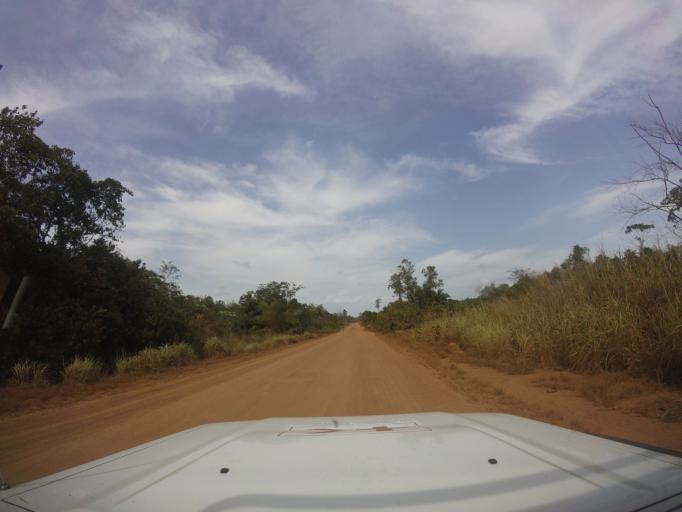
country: LR
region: Grand Cape Mount
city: Robertsport
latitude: 6.6985
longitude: -11.0978
